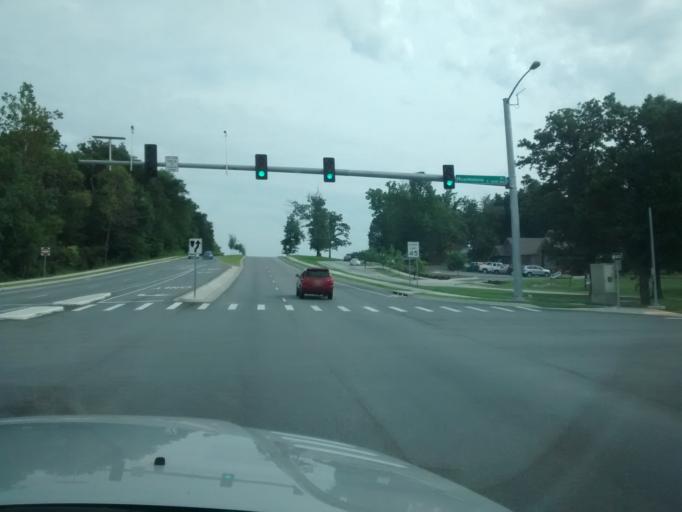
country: US
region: Arkansas
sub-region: Washington County
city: Johnson
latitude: 36.1362
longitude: -94.1178
